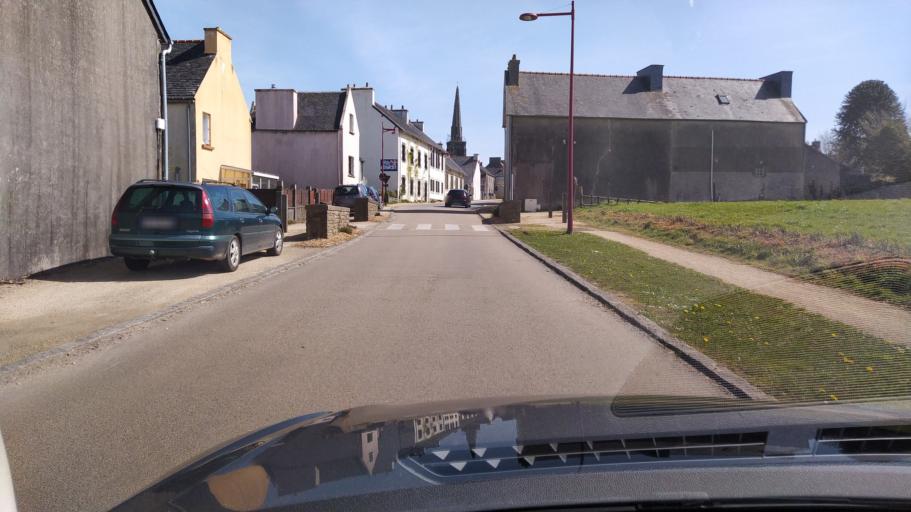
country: FR
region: Brittany
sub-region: Departement du Finistere
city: Plouneour-Menez
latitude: 48.4149
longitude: -3.9600
